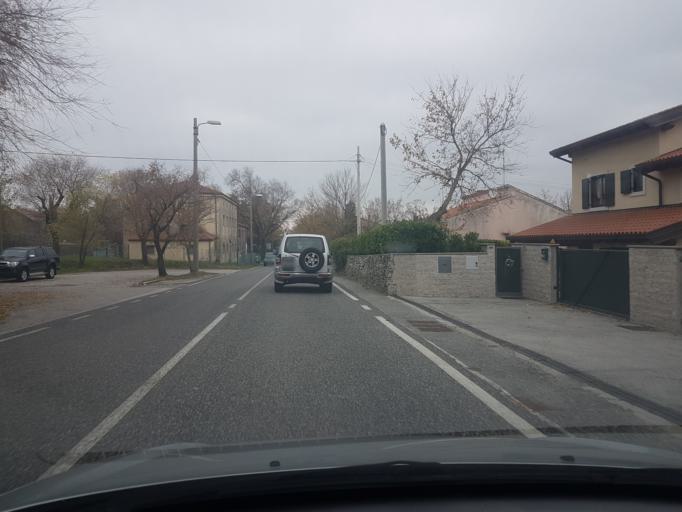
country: IT
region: Friuli Venezia Giulia
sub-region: Provincia di Trieste
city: Santa Croce
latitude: 45.7336
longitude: 13.6981
